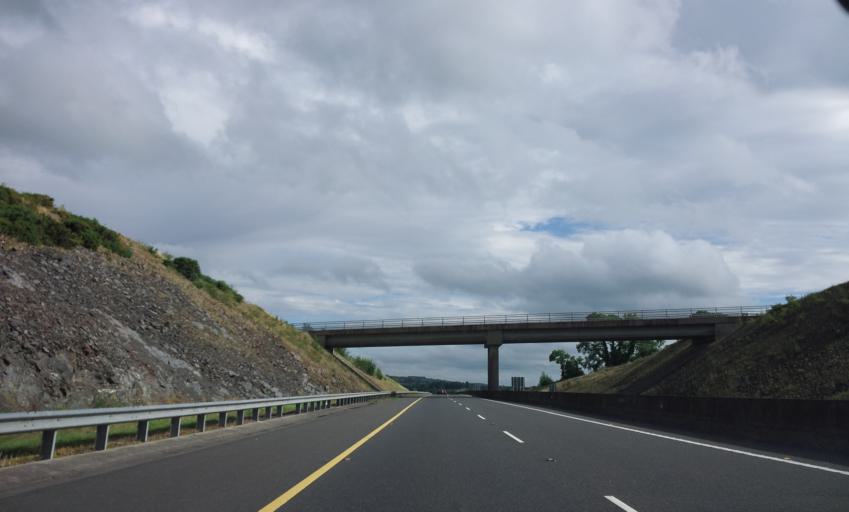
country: IE
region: Munster
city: Ballina
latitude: 52.7695
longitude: -8.3865
